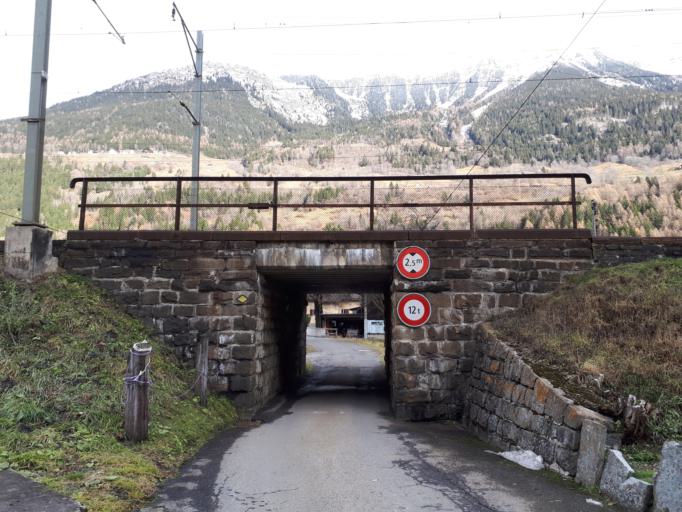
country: CH
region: Ticino
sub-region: Leventina District
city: Airolo
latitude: 46.5085
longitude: 8.7027
